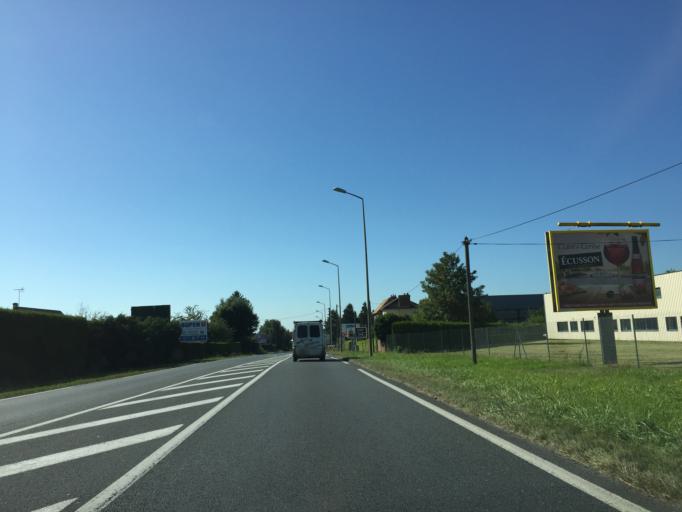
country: FR
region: Lower Normandy
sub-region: Departement du Calvados
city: Beuvillers
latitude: 49.1472
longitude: 0.2580
